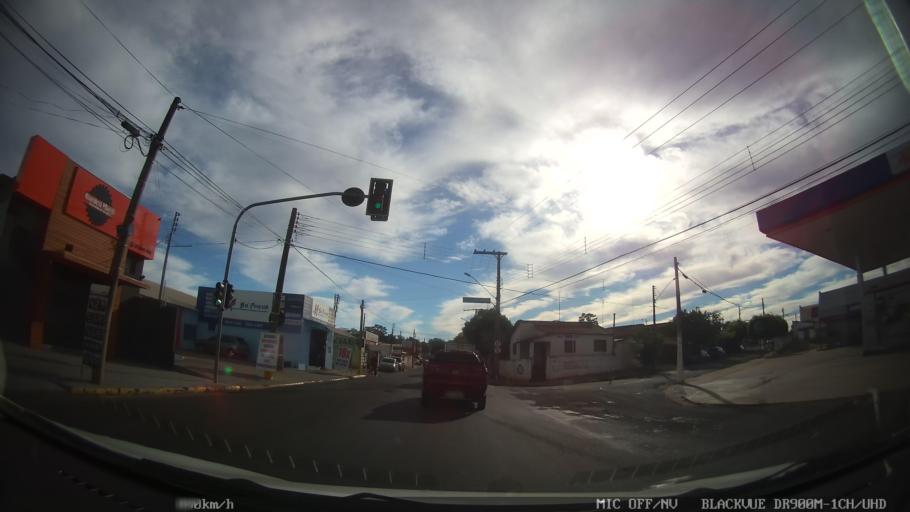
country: BR
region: Sao Paulo
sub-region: Catanduva
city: Catanduva
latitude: -21.1187
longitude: -48.9653
